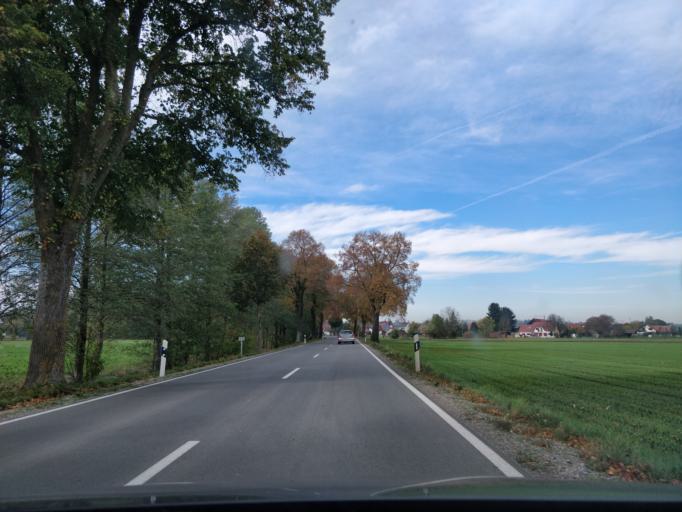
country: DE
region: Bavaria
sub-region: Swabia
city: Wiedergeltingen
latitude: 48.0355
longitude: 10.6838
